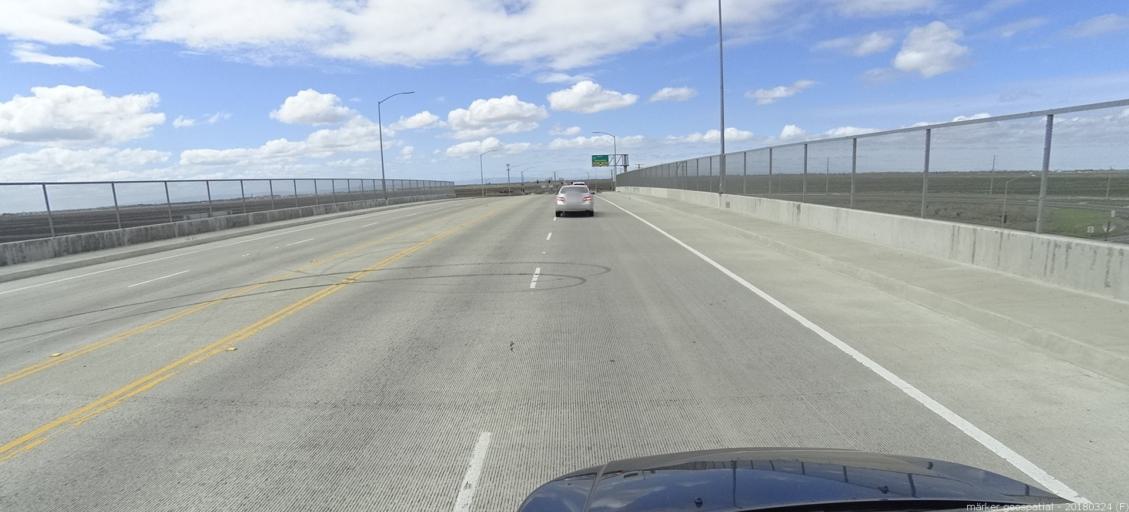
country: US
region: California
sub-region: Sacramento County
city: Elverta
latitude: 38.7143
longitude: -121.5399
